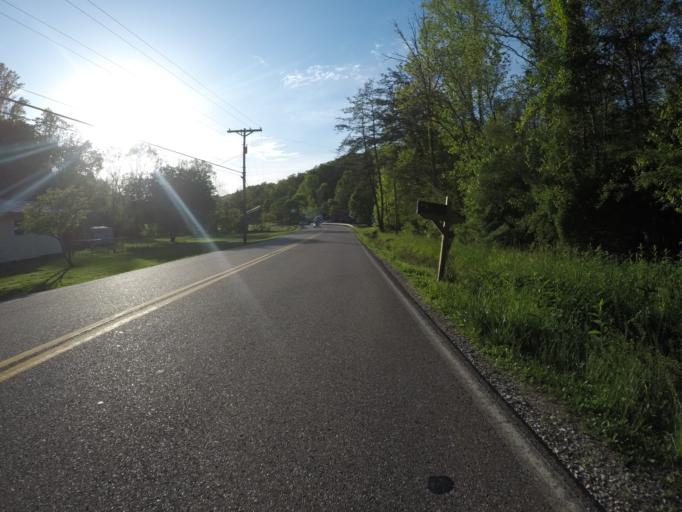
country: US
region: West Virginia
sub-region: Cabell County
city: Huntington
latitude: 38.5530
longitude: -82.4433
